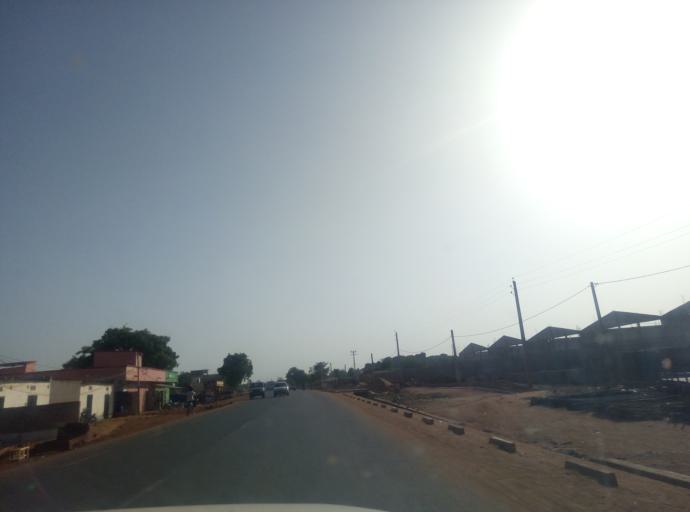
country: ML
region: Bamako
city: Bamako
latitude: 12.5860
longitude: -7.7688
